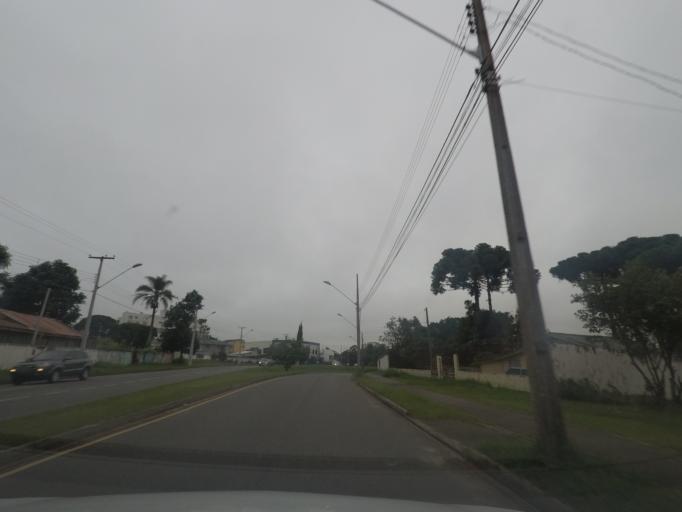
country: BR
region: Parana
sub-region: Curitiba
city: Curitiba
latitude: -25.4535
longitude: -49.2586
